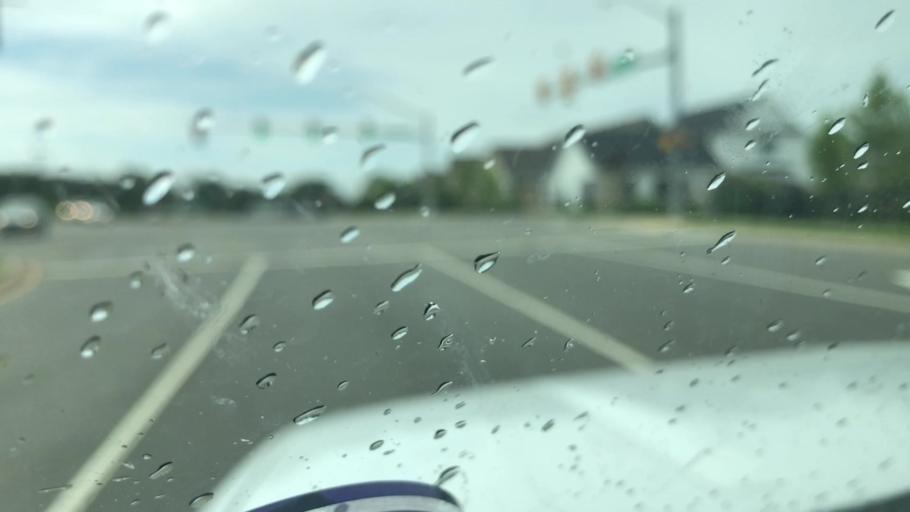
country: US
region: Virginia
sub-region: Henrico County
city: Short Pump
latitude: 37.6316
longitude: -77.6110
